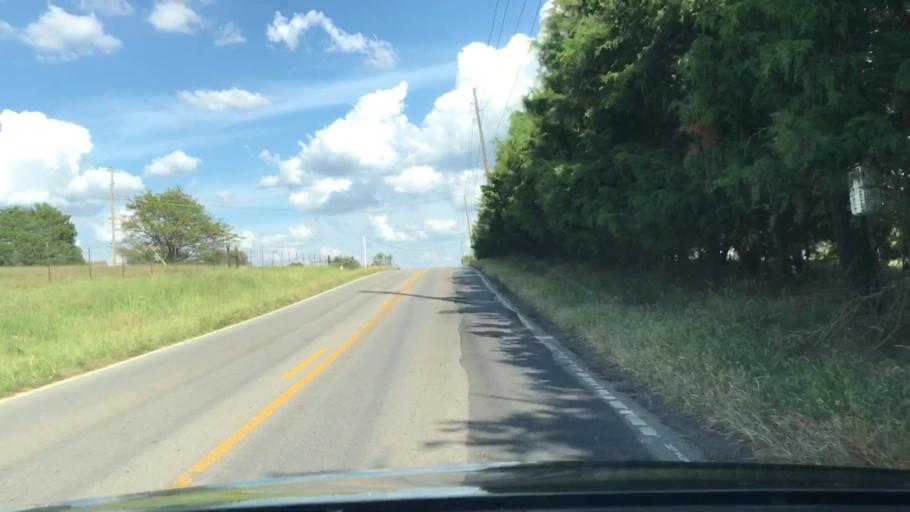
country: US
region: Alabama
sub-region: Madison County
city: Harvest
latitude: 34.8085
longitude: -86.7371
